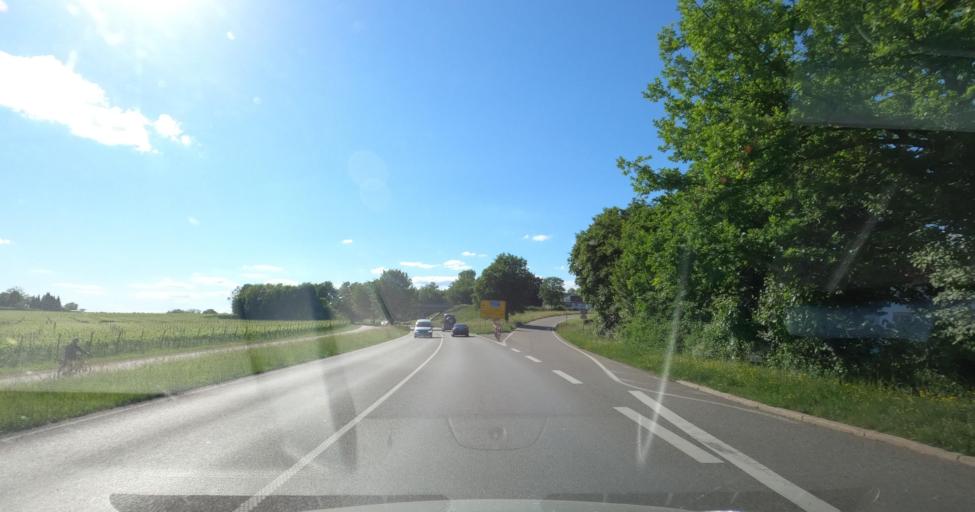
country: DE
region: Baden-Wuerttemberg
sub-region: Tuebingen Region
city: Stetten
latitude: 47.6881
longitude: 9.2981
